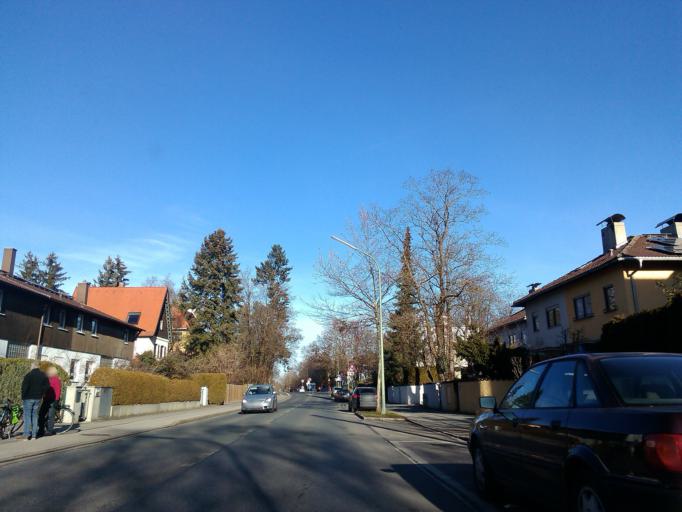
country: DE
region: Bavaria
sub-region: Upper Bavaria
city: Pasing
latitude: 48.1558
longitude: 11.4670
